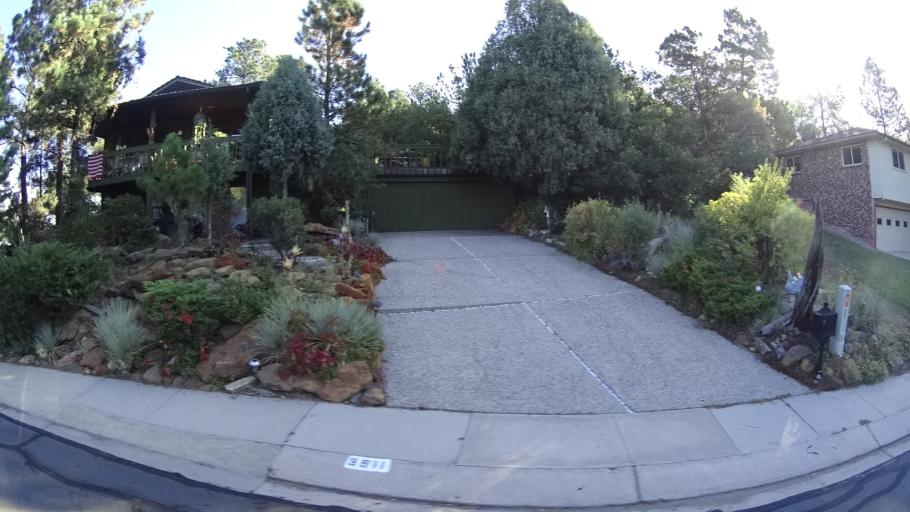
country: US
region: Colorado
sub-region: El Paso County
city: Colorado Springs
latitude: 38.8883
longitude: -104.7713
